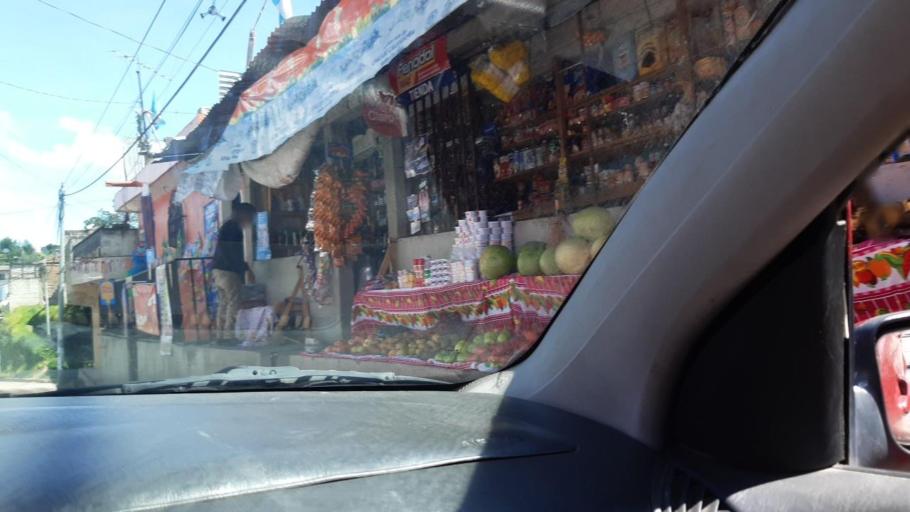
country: GT
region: Quetzaltenango
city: Salcaja
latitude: 14.8781
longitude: -91.4496
